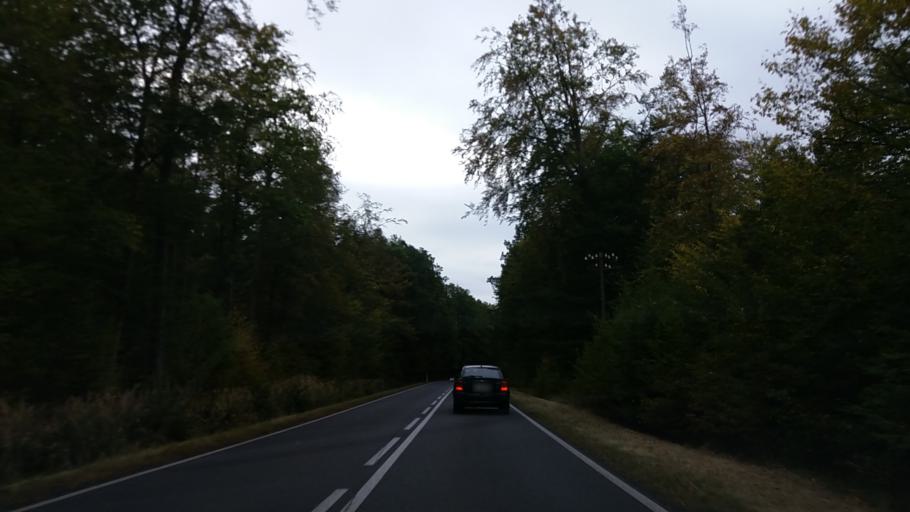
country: PL
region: Lubusz
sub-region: Powiat gorzowski
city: Klodawa
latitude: 52.8270
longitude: 15.2123
